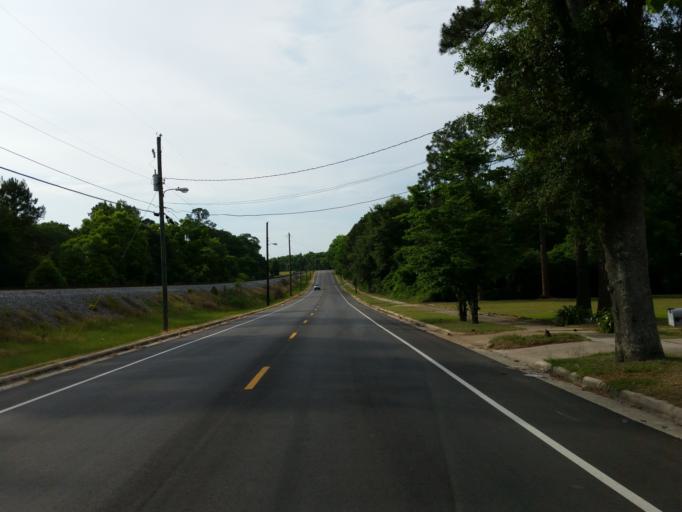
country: US
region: Georgia
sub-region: Turner County
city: Ashburn
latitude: 31.7120
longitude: -83.6566
